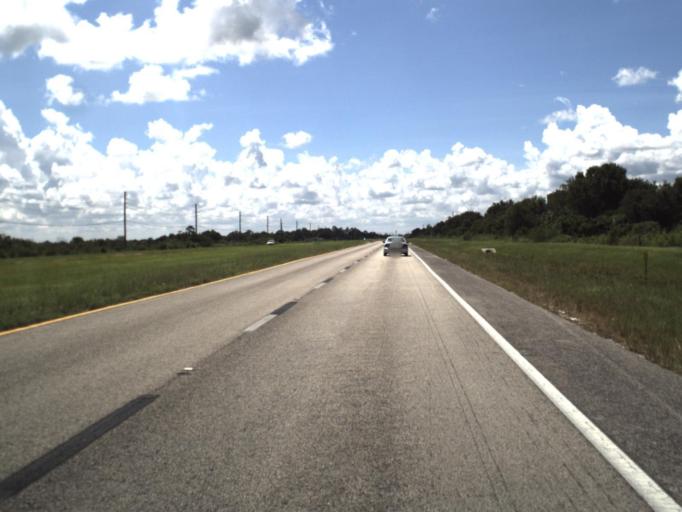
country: US
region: Florida
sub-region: Charlotte County
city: Harbour Heights
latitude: 27.0133
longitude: -81.9588
